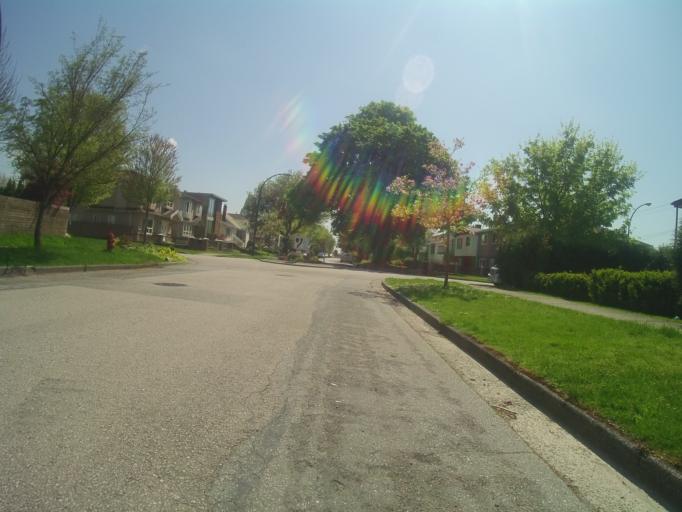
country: CA
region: British Columbia
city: Vancouver
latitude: 49.2352
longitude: -123.0798
